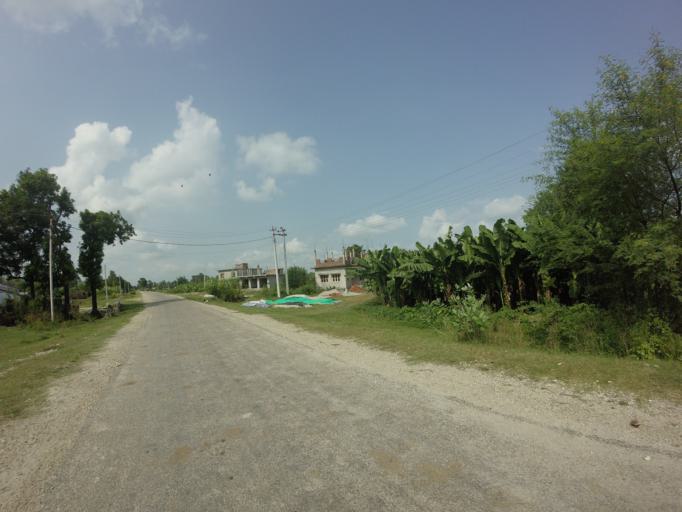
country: NP
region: Far Western
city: Tikapur
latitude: 28.4637
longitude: 81.0758
